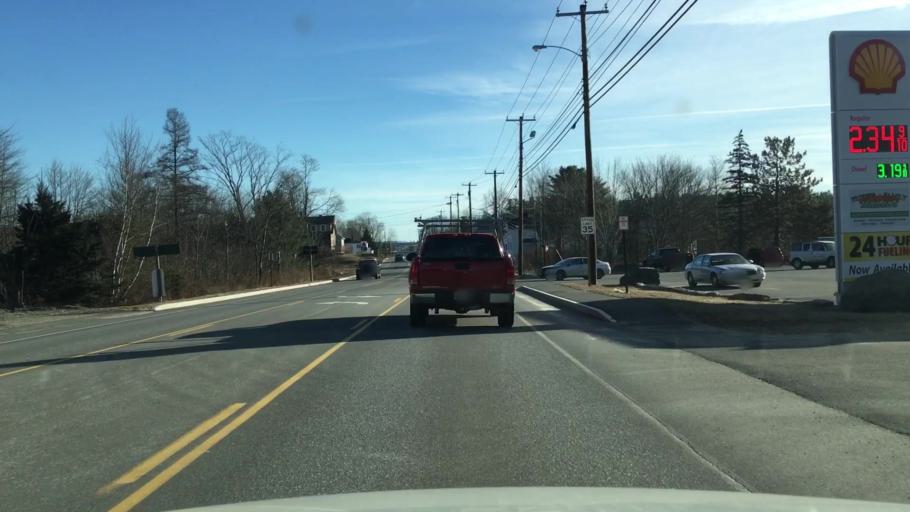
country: US
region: Maine
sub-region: Hancock County
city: Ellsworth
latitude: 44.5602
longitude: -68.4367
